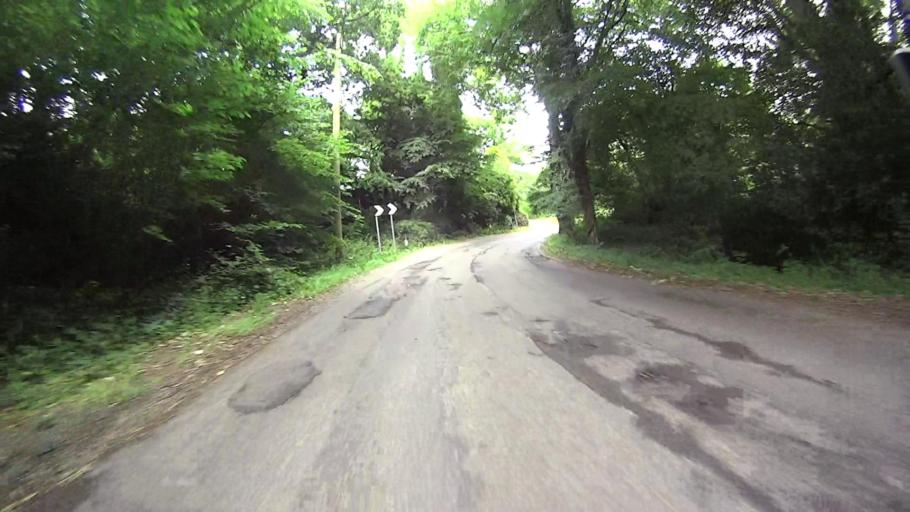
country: GB
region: England
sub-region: West Sussex
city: Bewbush
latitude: 51.1245
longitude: -0.2627
